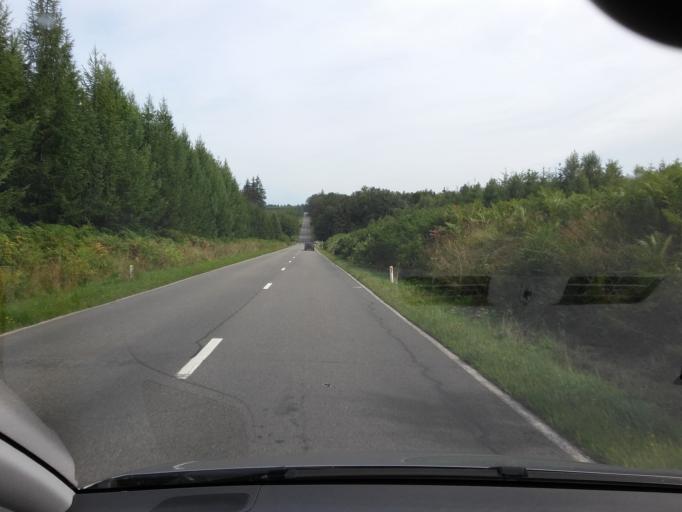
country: BE
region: Wallonia
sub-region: Province du Luxembourg
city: Chiny
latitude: 49.7588
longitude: 5.3174
